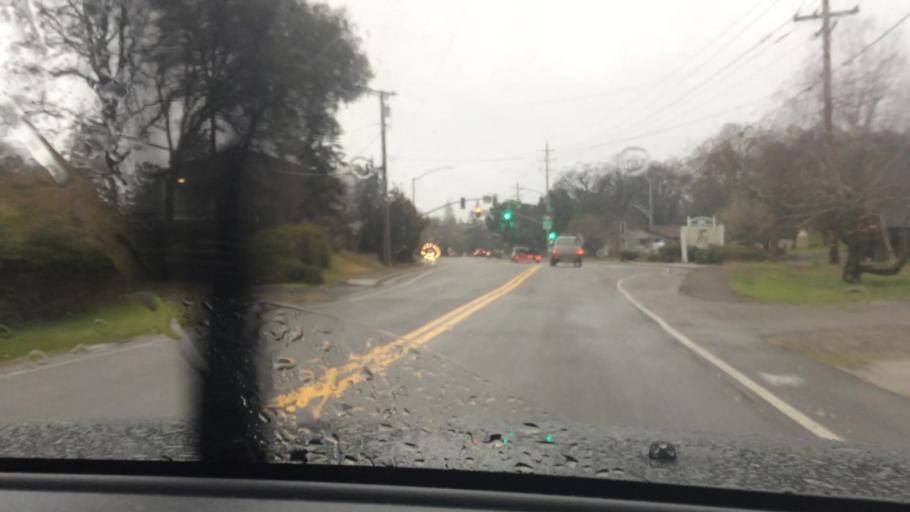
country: US
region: California
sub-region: El Dorado County
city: Deer Park
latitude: 38.6821
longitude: -120.8405
